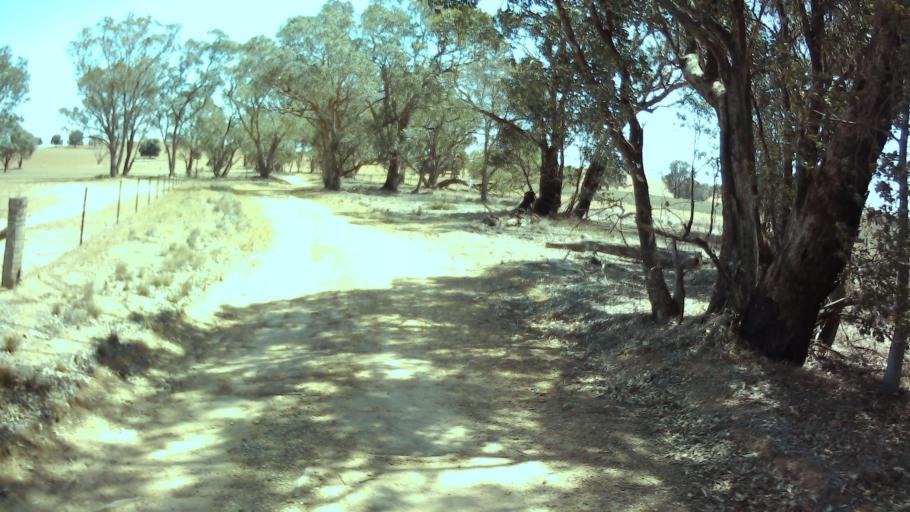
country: AU
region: New South Wales
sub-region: Weddin
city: Grenfell
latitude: -33.9877
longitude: 148.1645
